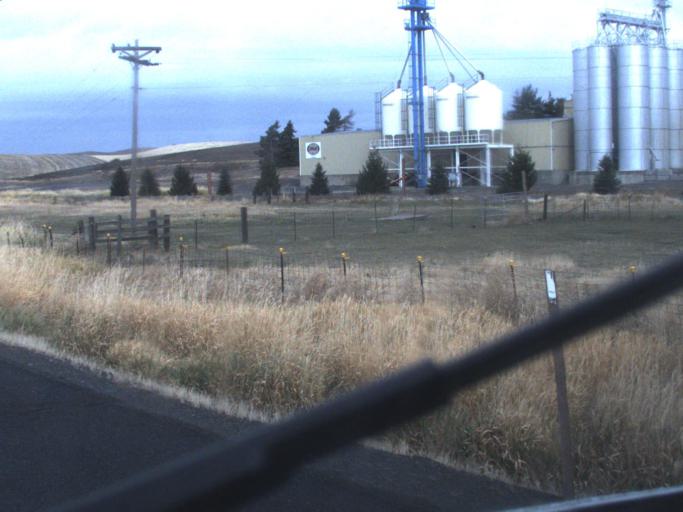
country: US
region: Washington
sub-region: Whitman County
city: Pullman
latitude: 46.6428
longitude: -117.1854
